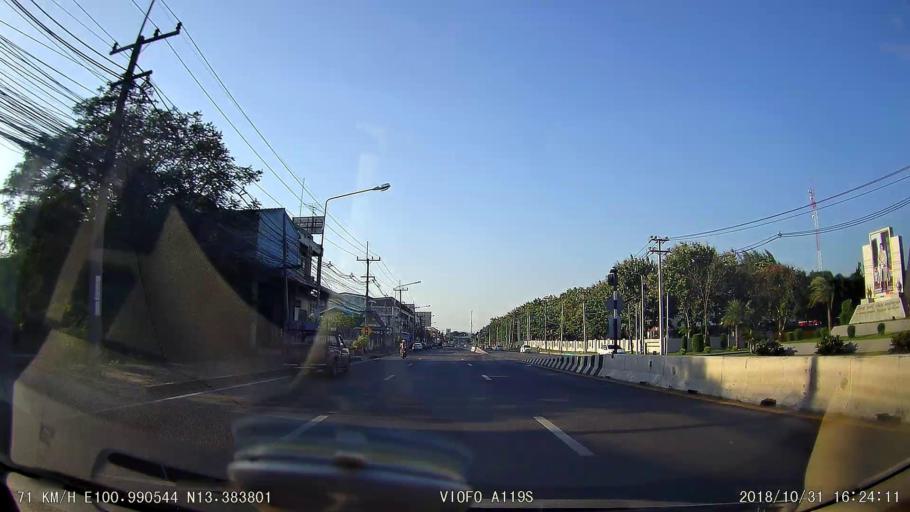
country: TH
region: Chon Buri
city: Chon Buri
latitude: 13.3840
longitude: 100.9904
